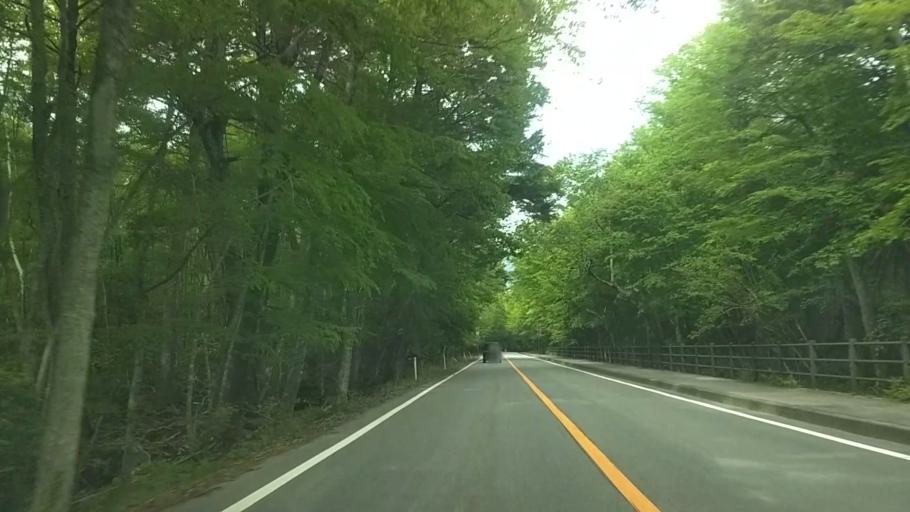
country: JP
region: Yamanashi
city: Fujikawaguchiko
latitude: 35.4888
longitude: 138.6451
